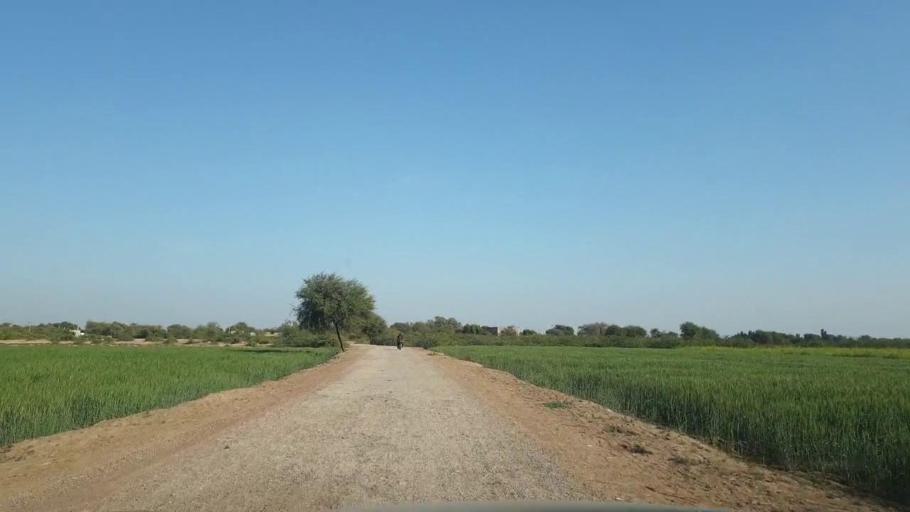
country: PK
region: Sindh
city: Tando Adam
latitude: 25.6871
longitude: 68.6769
